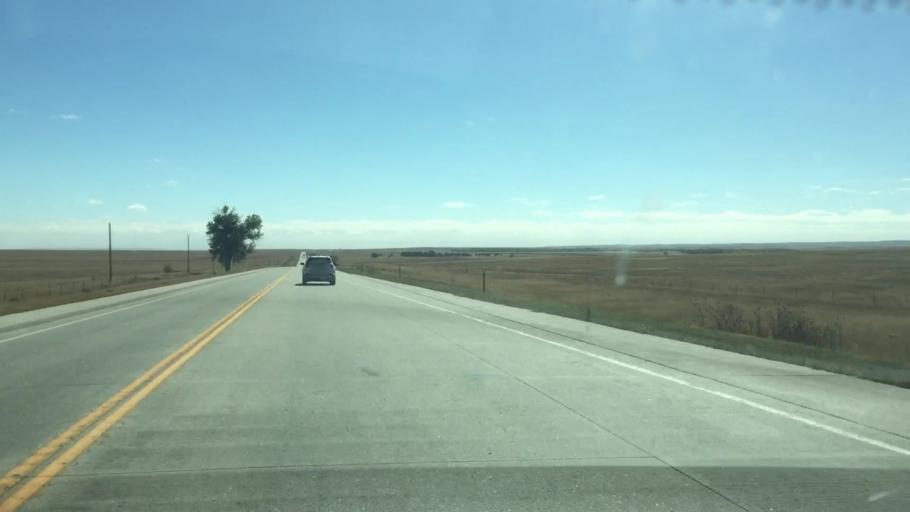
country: US
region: Colorado
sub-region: Lincoln County
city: Limon
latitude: 39.2095
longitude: -103.5951
